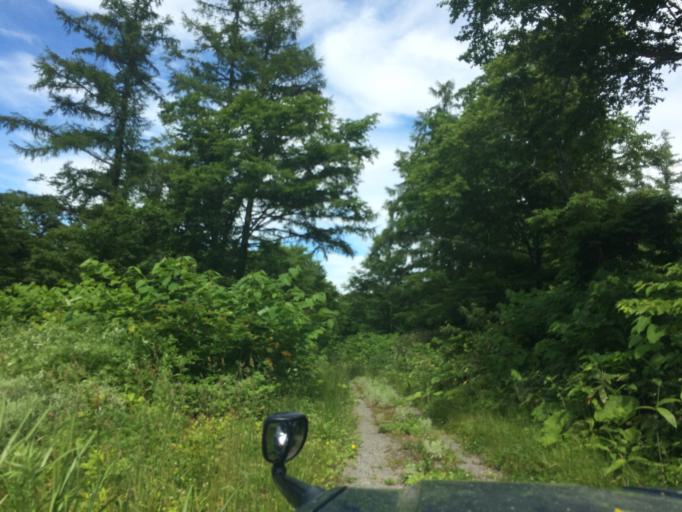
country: JP
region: Hokkaido
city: Niseko Town
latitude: 42.8611
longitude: 140.7965
